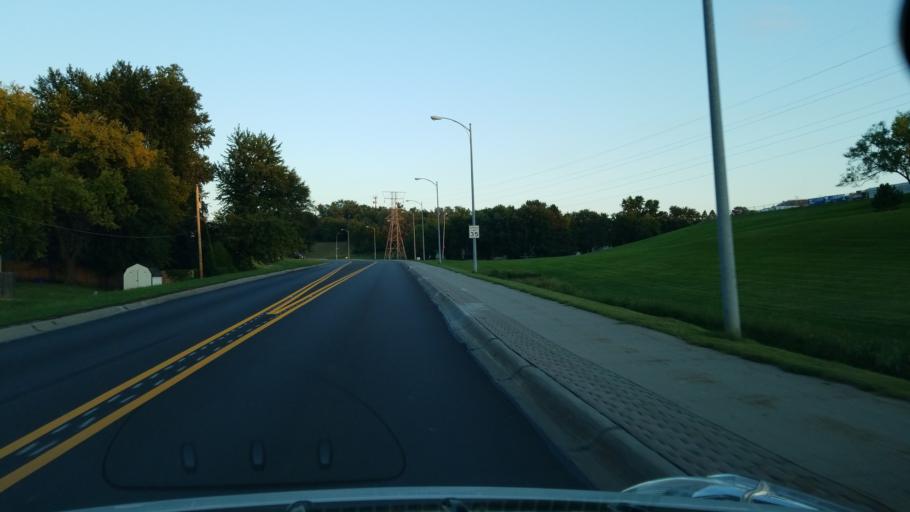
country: US
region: Nebraska
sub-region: Sarpy County
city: Bellevue
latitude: 41.1491
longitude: -95.9040
